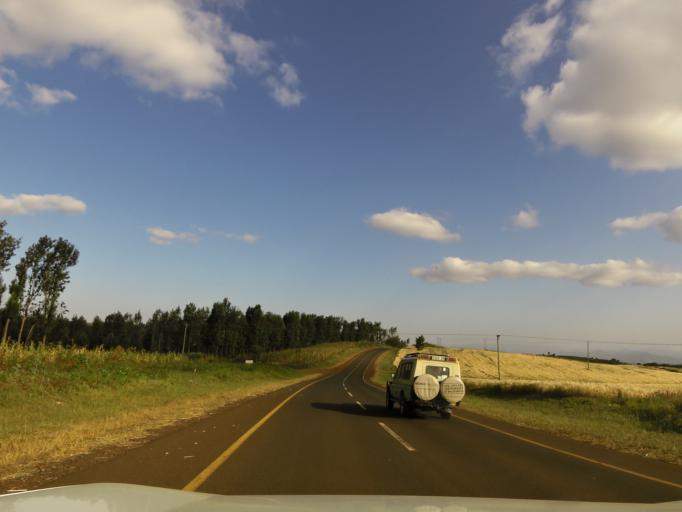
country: TZ
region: Arusha
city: Kiratu
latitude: -3.3241
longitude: 35.6008
